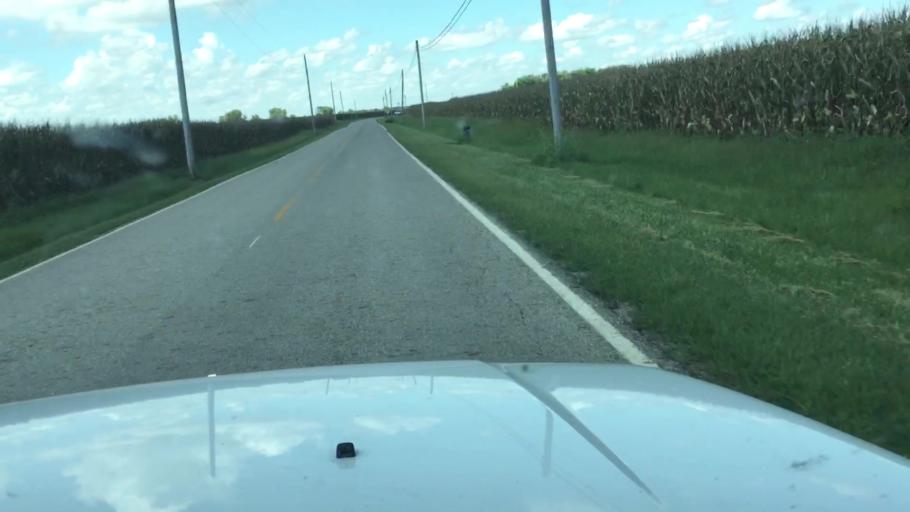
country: US
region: Ohio
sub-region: Madison County
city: Mount Sterling
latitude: 39.6961
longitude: -83.2425
